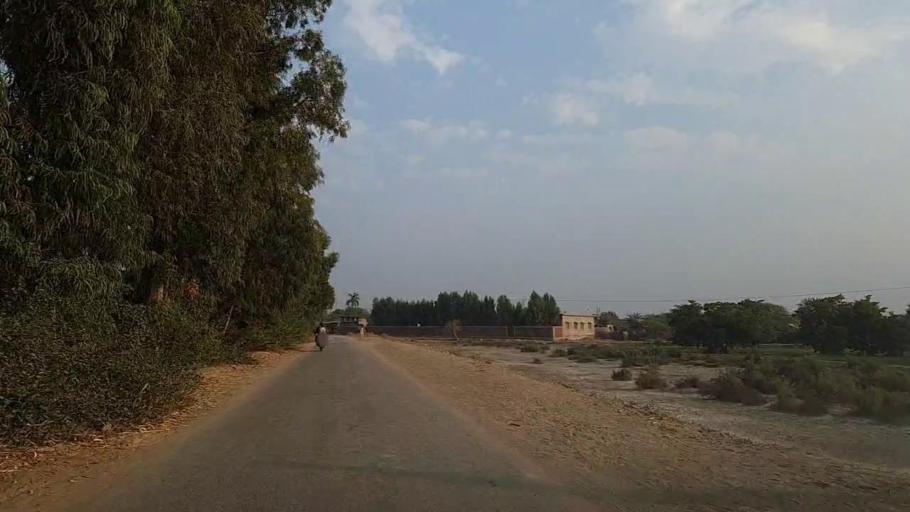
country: PK
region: Sindh
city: Samaro
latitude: 25.2878
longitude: 69.2376
